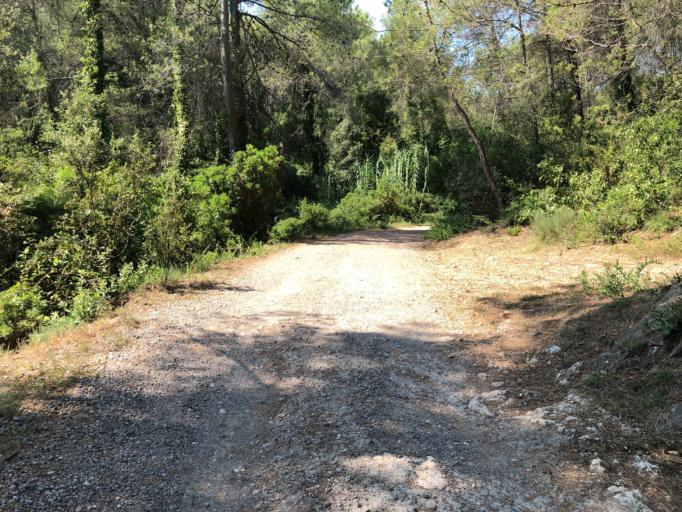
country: ES
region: Catalonia
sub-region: Provincia de Barcelona
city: Corbera de Llobregat
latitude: 41.4199
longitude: 1.9035
